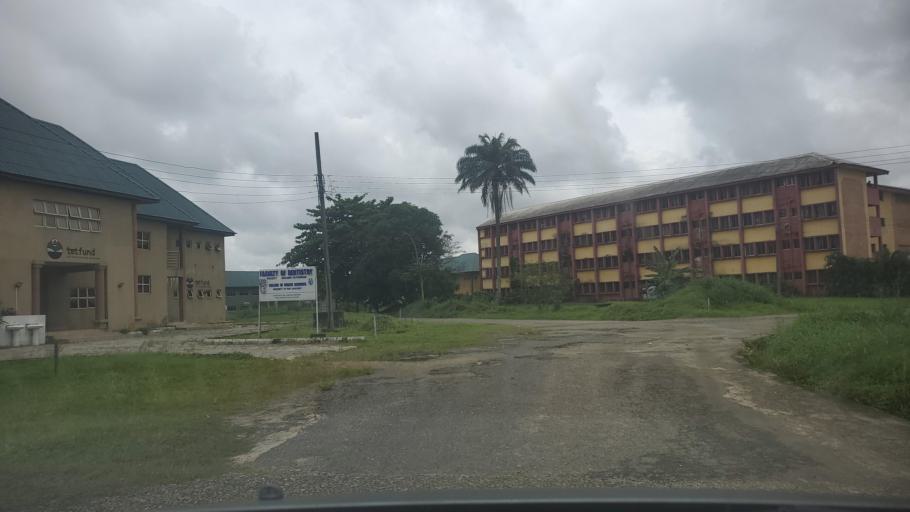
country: NG
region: Rivers
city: Emuoha
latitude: 4.9021
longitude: 6.9256
